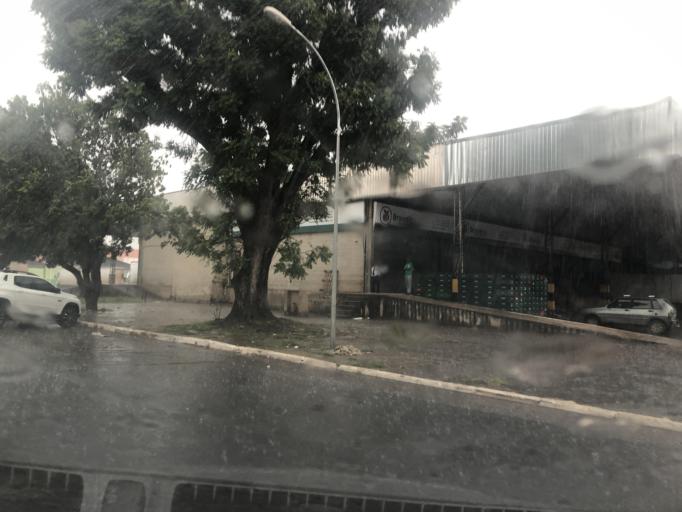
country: BR
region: Federal District
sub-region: Brasilia
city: Brasilia
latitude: -15.7928
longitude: -47.9474
